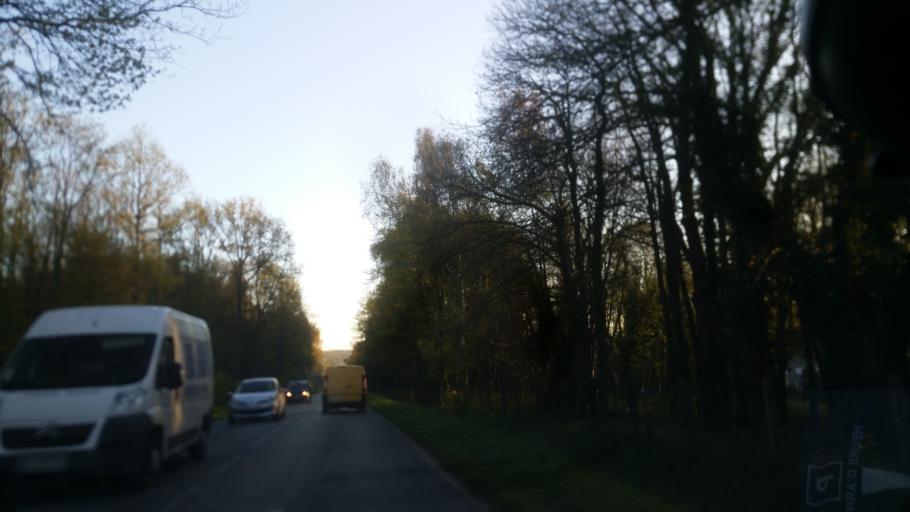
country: FR
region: Ile-de-France
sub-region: Departement de l'Essonne
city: Angervilliers
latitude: 48.5965
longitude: 2.0655
